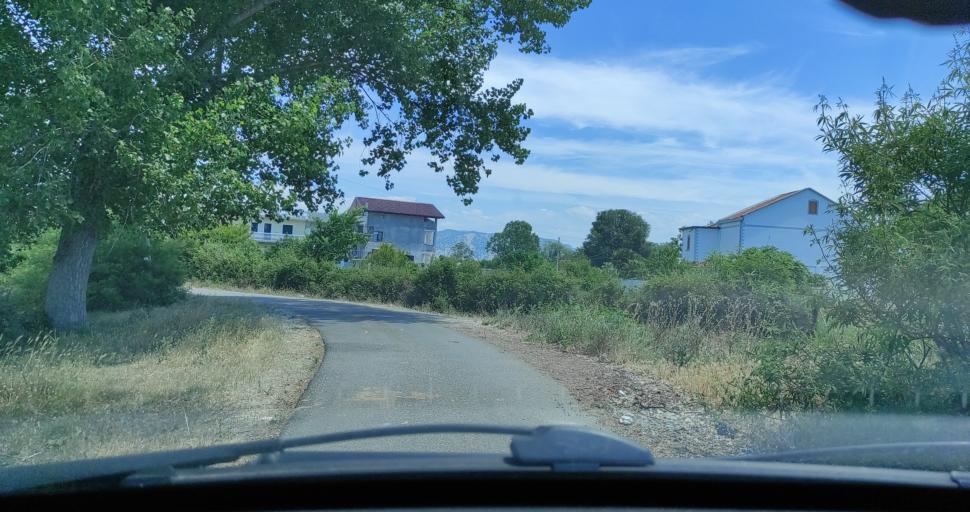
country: AL
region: Shkoder
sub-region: Rrethi i Shkodres
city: Velipoje
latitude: 41.8736
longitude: 19.3789
